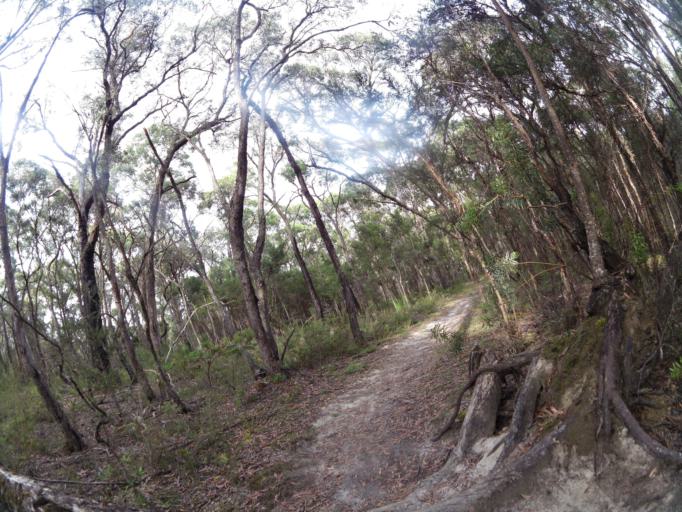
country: AU
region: Victoria
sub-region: Colac-Otway
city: Colac
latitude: -38.4882
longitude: 143.7037
